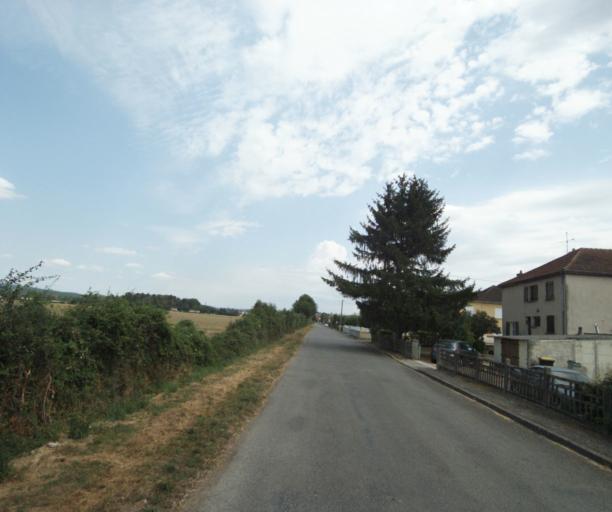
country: FR
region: Bourgogne
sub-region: Departement de Saone-et-Loire
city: Gueugnon
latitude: 46.6094
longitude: 4.0516
